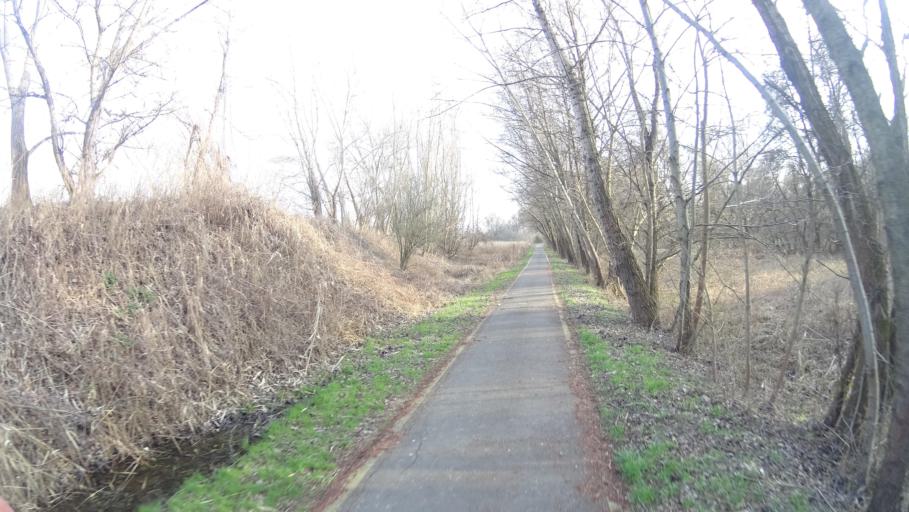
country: HU
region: Pest
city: Vac
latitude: 47.7604
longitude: 19.1370
